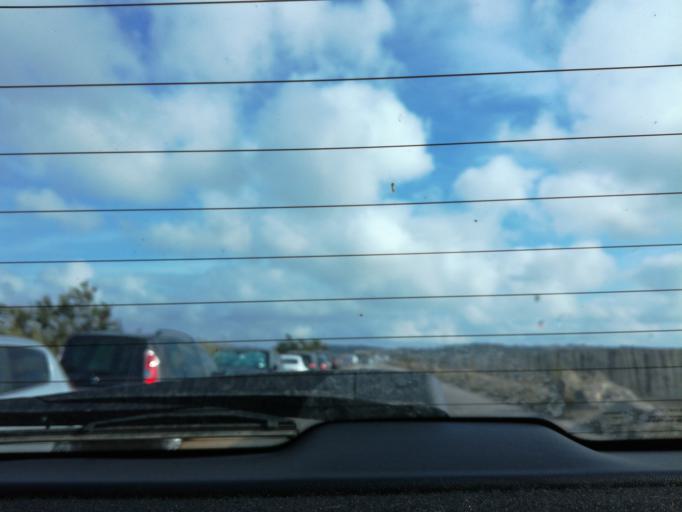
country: FR
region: Provence-Alpes-Cote d'Azur
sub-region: Departement du Var
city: Hyeres
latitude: 43.0590
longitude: 6.1330
